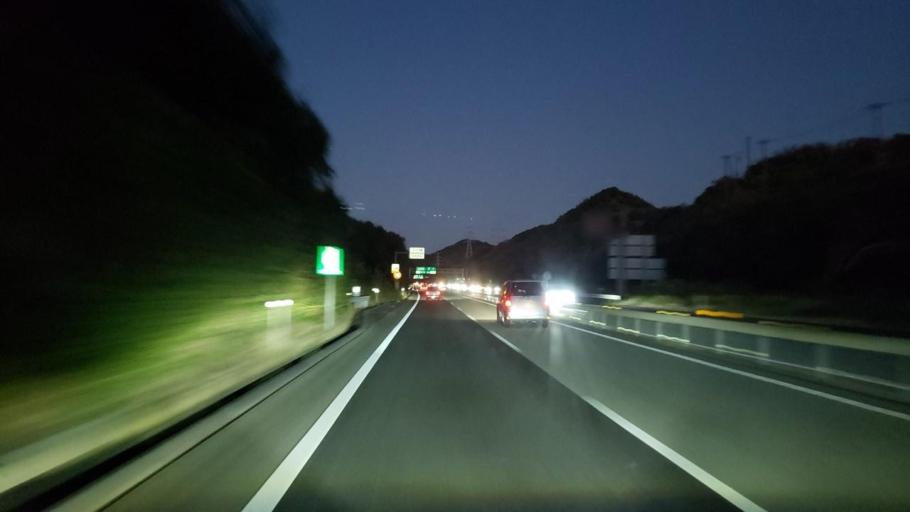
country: JP
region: Hyogo
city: Fukura
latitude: 34.2476
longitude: 134.6693
